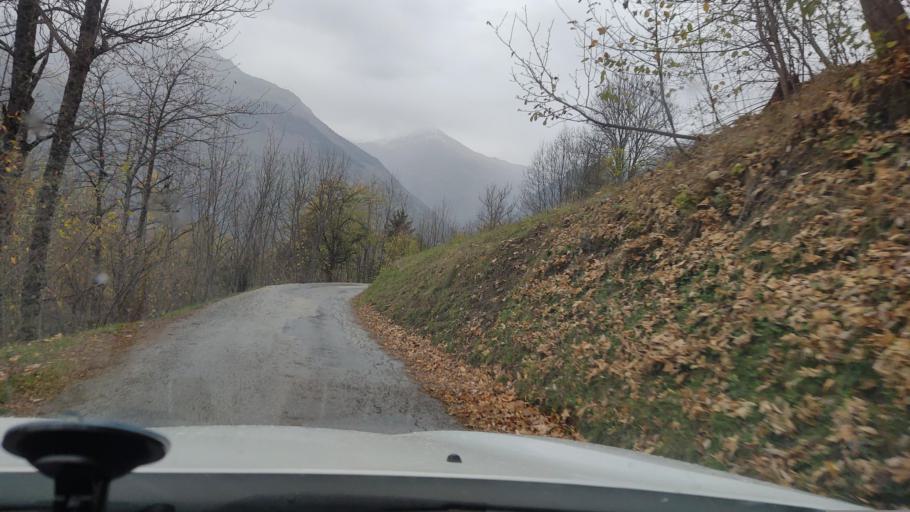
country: FR
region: Rhone-Alpes
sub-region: Departement de la Savoie
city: Bourg-Saint-Maurice
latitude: 45.5996
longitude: 6.7745
